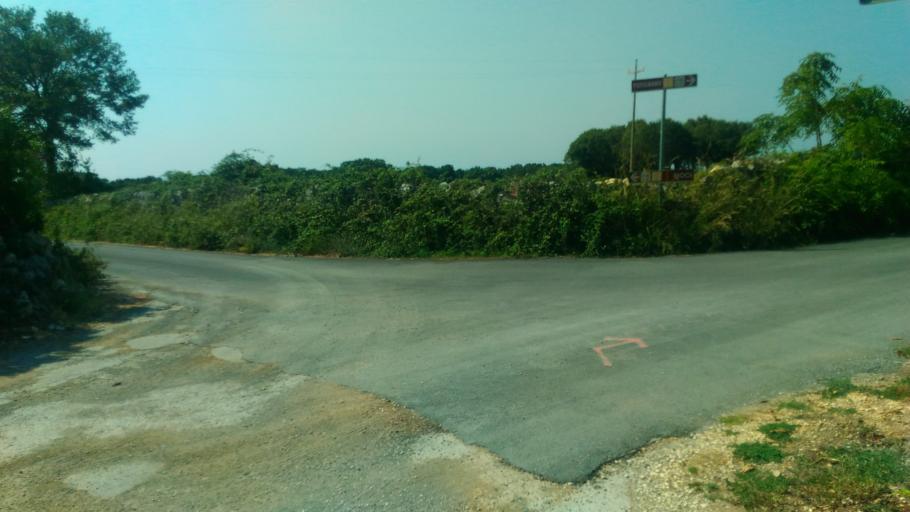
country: IT
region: Apulia
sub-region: Provincia di Bari
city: Alberobello
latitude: 40.8014
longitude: 17.1838
